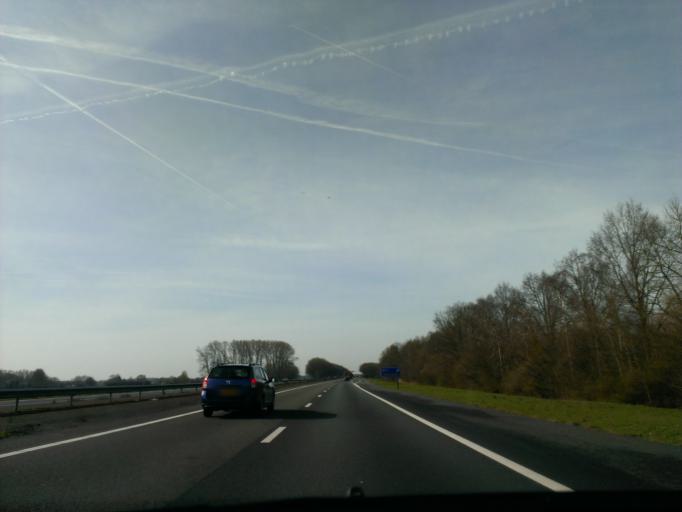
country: NL
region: Gelderland
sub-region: Gemeente Ermelo
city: Horst
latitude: 52.2731
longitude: 5.5398
